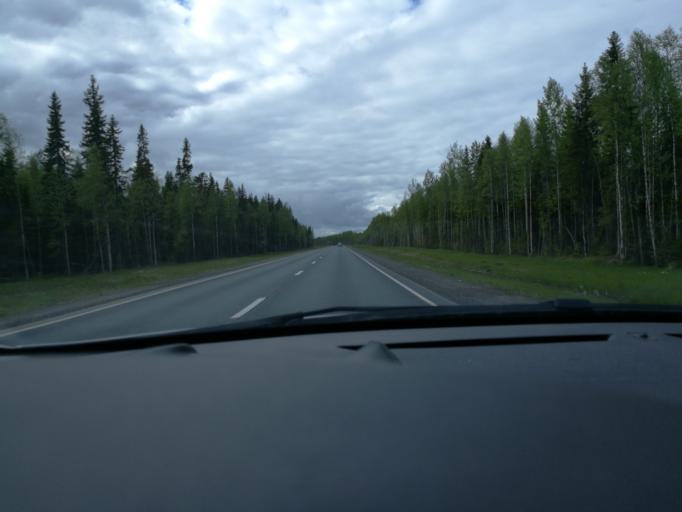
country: RU
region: Arkhangelskaya
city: Kholmogory
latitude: 64.2058
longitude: 41.2726
